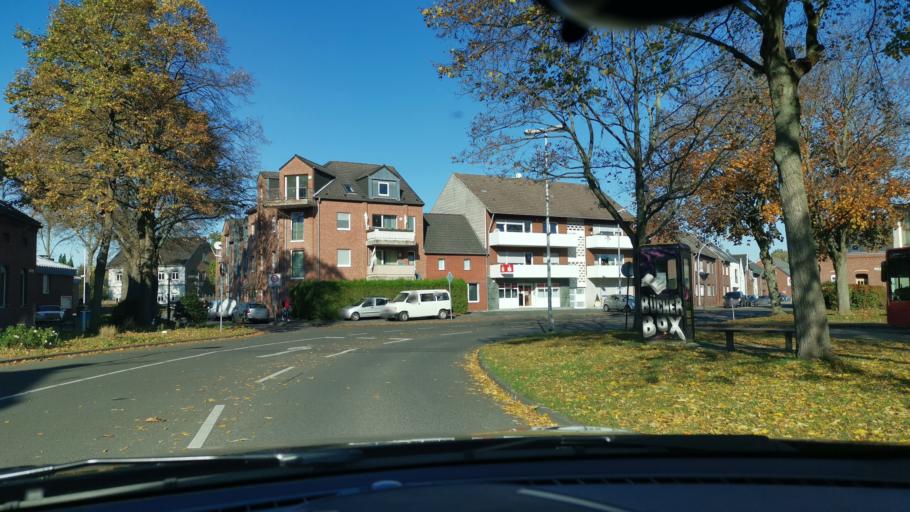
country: DE
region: North Rhine-Westphalia
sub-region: Regierungsbezirk Dusseldorf
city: Grevenbroich
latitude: 51.0660
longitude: 6.6281
